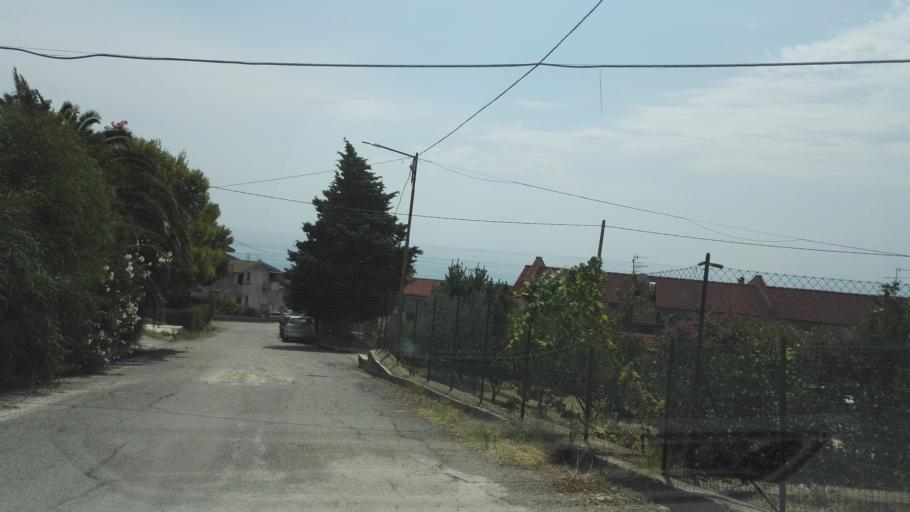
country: IT
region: Calabria
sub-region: Provincia di Reggio Calabria
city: Riace Marina
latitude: 38.3916
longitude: 16.5254
